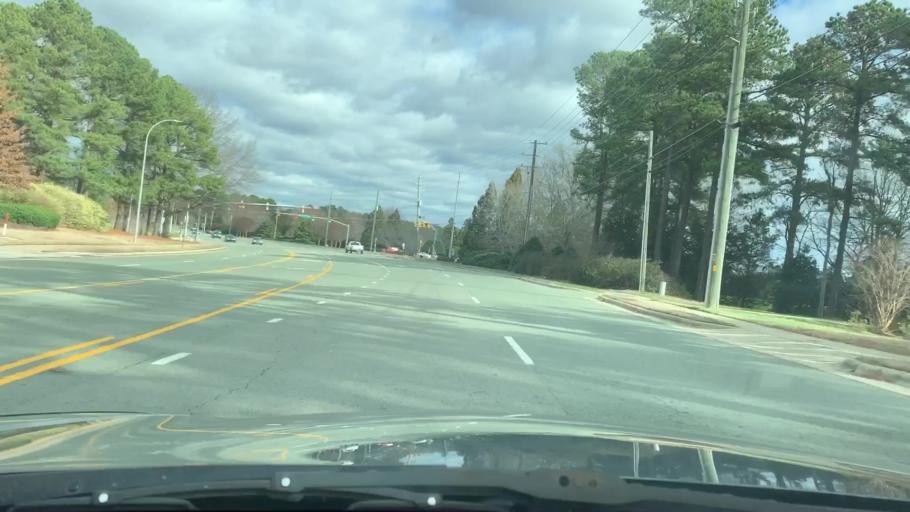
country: US
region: North Carolina
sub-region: Wake County
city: Cary
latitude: 35.8181
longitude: -78.7720
